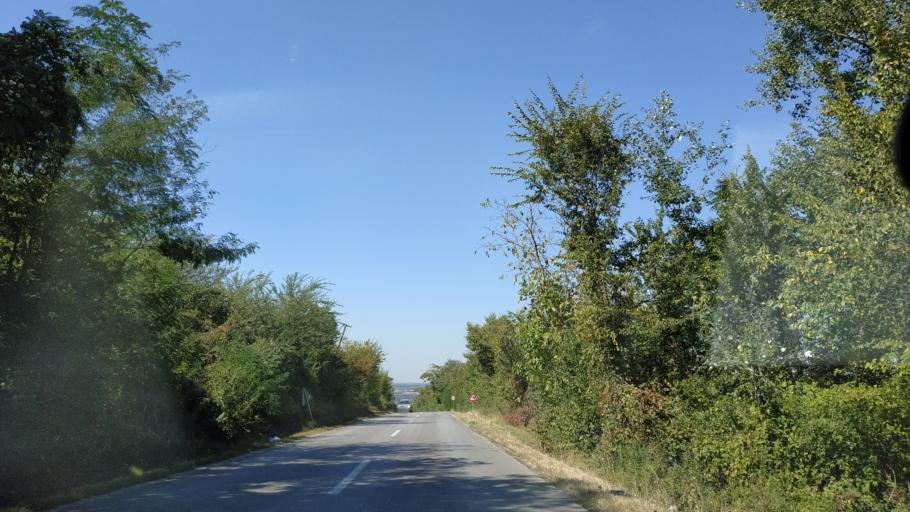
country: RS
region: Central Serbia
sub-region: Sumadijski Okrug
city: Raca
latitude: 44.2382
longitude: 20.8428
